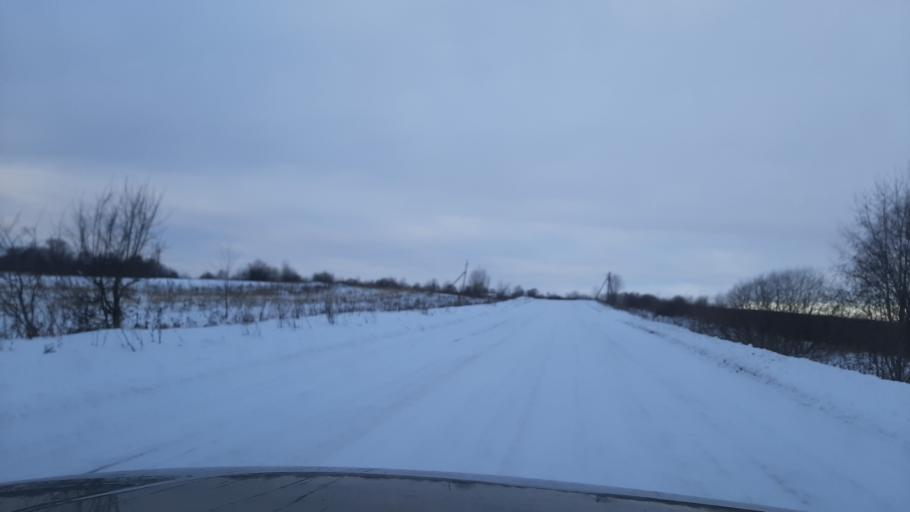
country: RU
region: Kostroma
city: Volgorechensk
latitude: 57.4487
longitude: 40.9793
